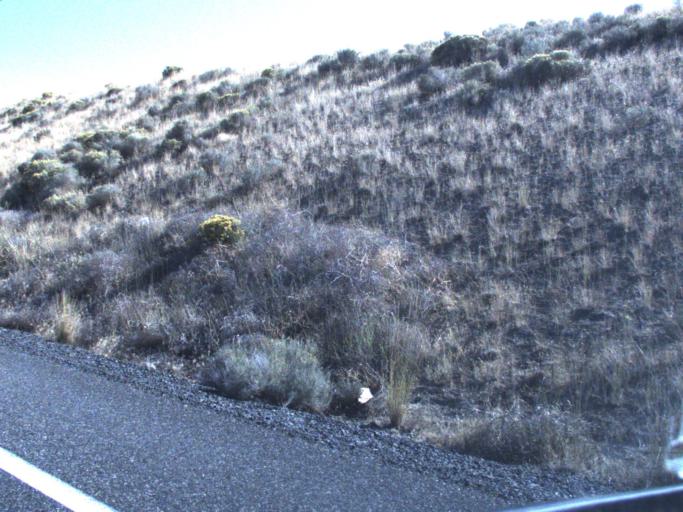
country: US
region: Washington
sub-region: Benton County
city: Highland
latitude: 46.1457
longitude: -119.1155
